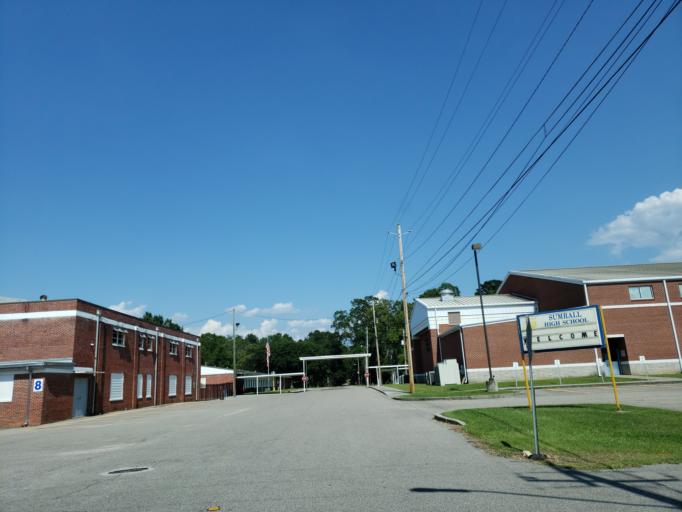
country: US
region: Mississippi
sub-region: Lamar County
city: Sumrall
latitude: 31.4175
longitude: -89.5424
